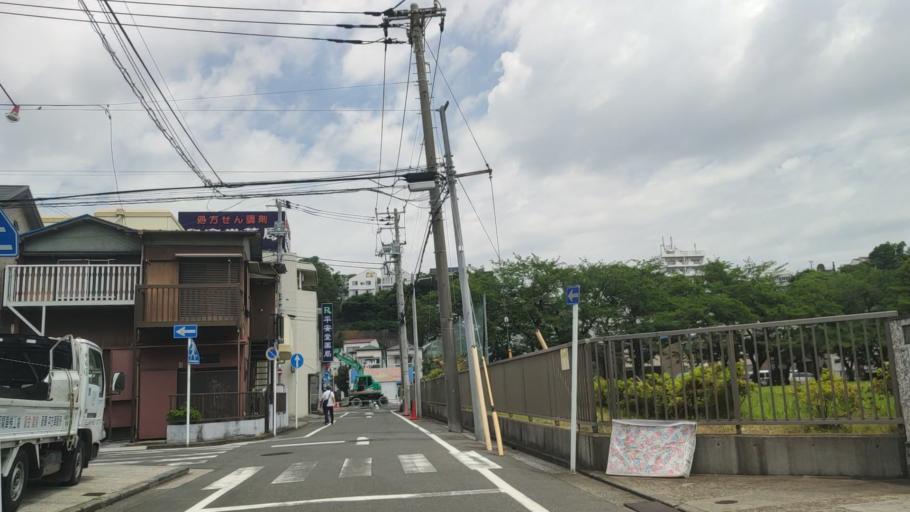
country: JP
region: Kanagawa
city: Yokohama
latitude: 35.4175
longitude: 139.6411
